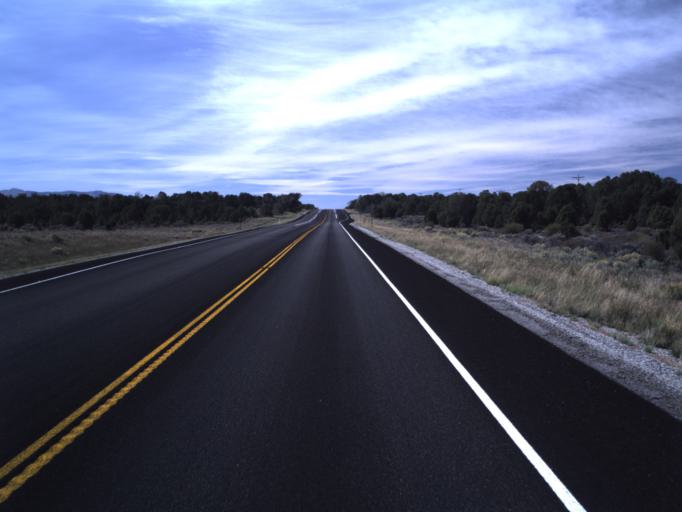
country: US
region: Colorado
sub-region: Dolores County
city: Dove Creek
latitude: 37.8371
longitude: -109.1136
